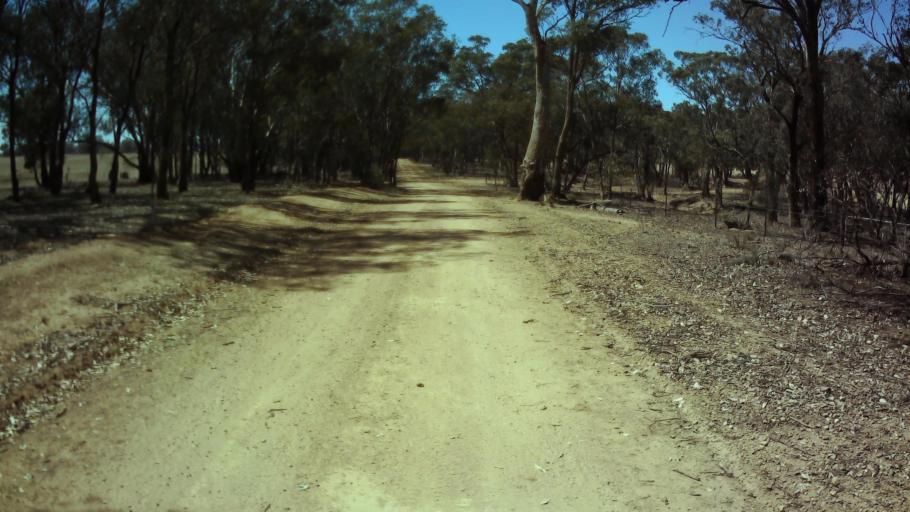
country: AU
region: New South Wales
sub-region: Weddin
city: Grenfell
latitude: -33.9592
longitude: 148.0864
